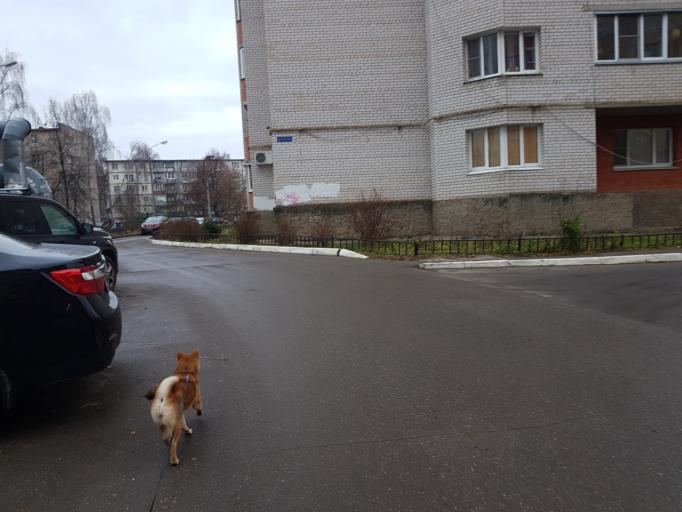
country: RU
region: Moskovskaya
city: Istra
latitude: 55.9082
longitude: 36.8694
